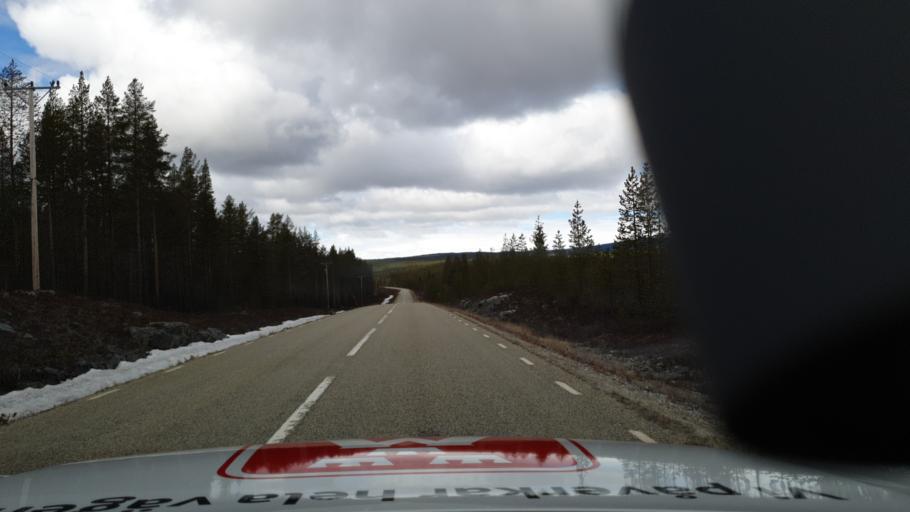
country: SE
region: Jaemtland
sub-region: Are Kommun
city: Jarpen
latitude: 62.8036
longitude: 13.6665
